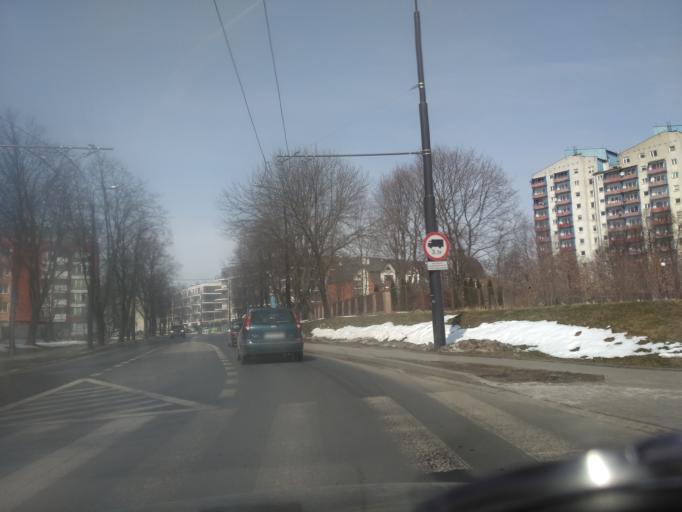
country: PL
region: Lublin Voivodeship
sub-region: Powiat lubelski
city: Lublin
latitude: 51.2565
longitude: 22.5749
